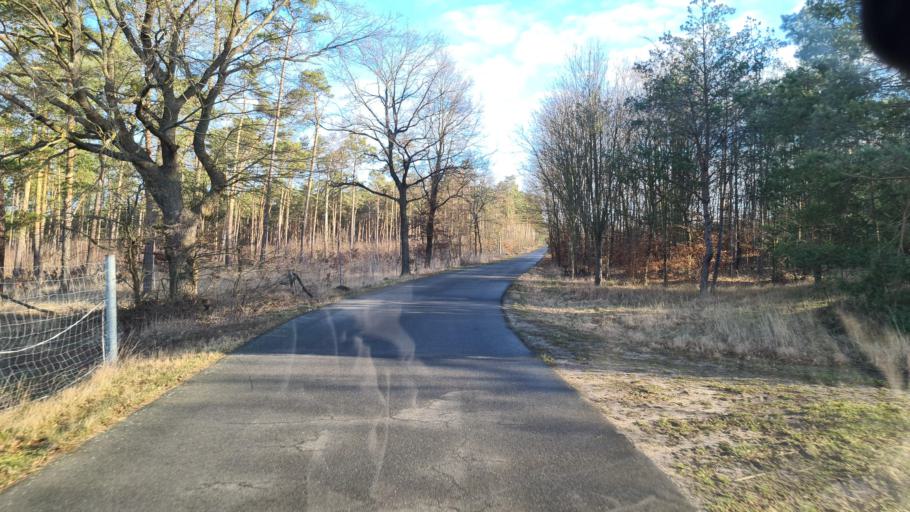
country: DE
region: Brandenburg
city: Herzberg
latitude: 51.6988
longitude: 13.1775
